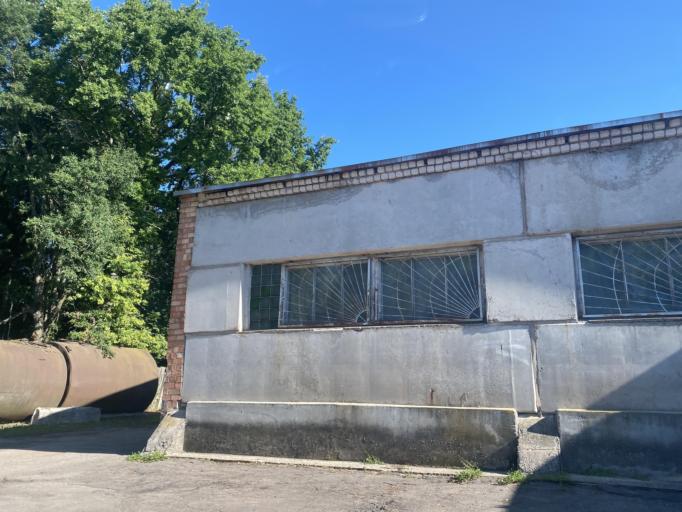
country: BY
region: Minsk
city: Zhdanovichy
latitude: 53.9125
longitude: 27.3722
